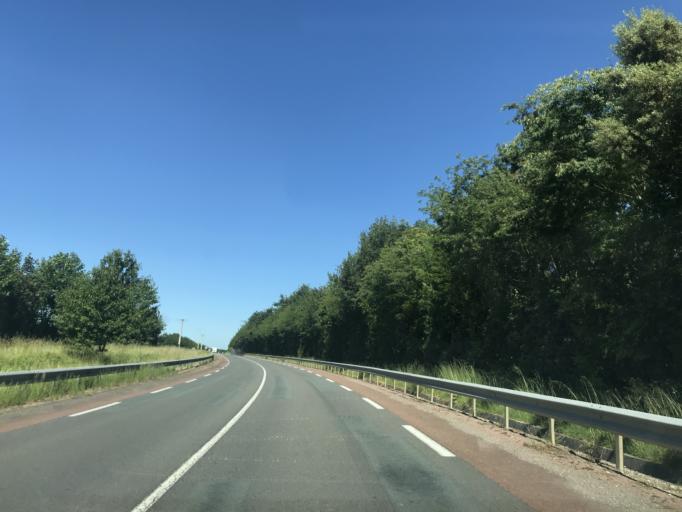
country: FR
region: Poitou-Charentes
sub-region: Departement de la Charente-Maritime
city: Gemozac
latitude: 45.5738
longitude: -0.6595
